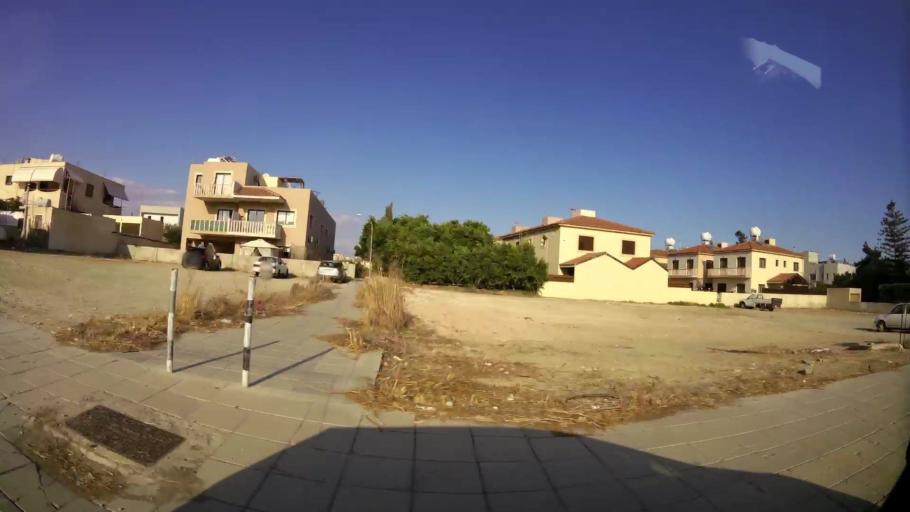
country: CY
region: Larnaka
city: Livadia
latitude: 34.9390
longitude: 33.6102
